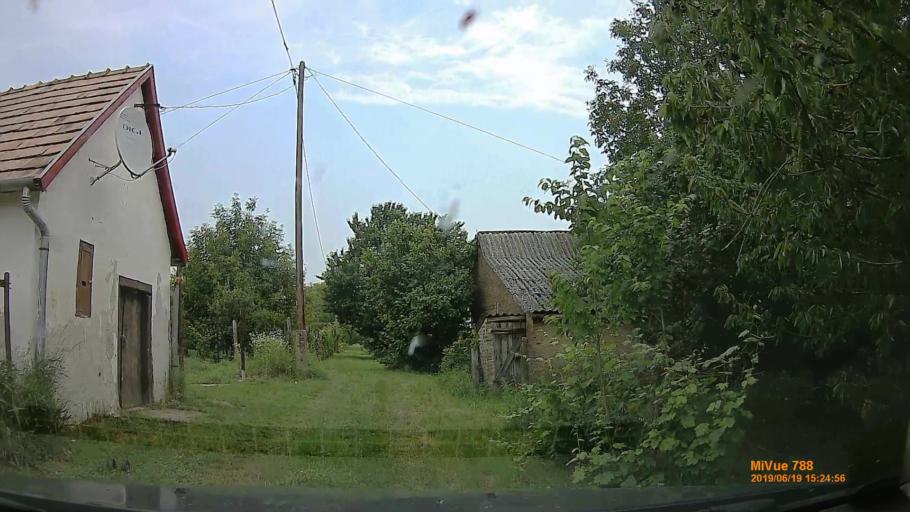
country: HU
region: Baranya
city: Szigetvar
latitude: 46.0738
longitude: 17.8477
